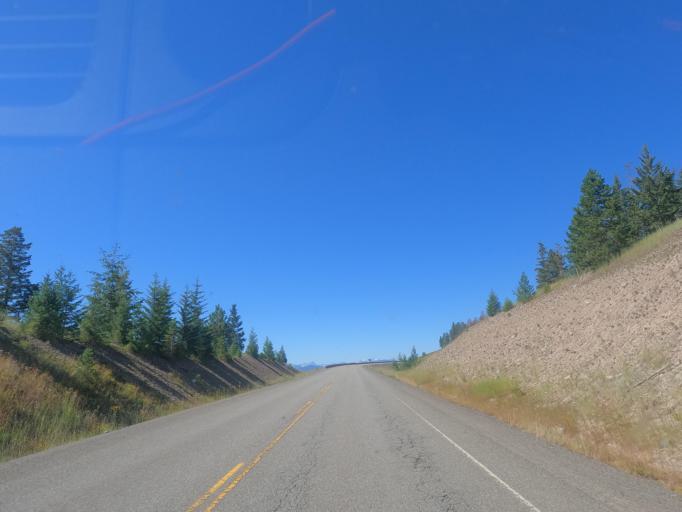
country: CA
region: British Columbia
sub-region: Thompson-Nicola Regional District
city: Ashcroft
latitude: 50.5720
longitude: -121.1774
